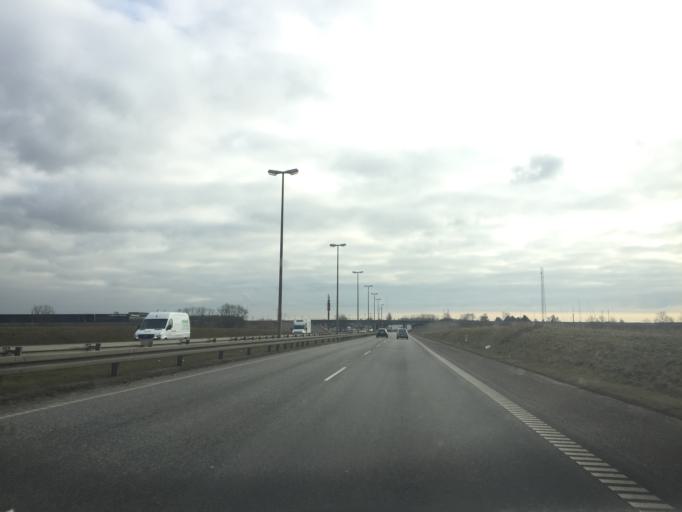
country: DK
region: Capital Region
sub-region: Hoje-Taastrup Kommune
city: Taastrup
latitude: 55.6249
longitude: 12.3147
